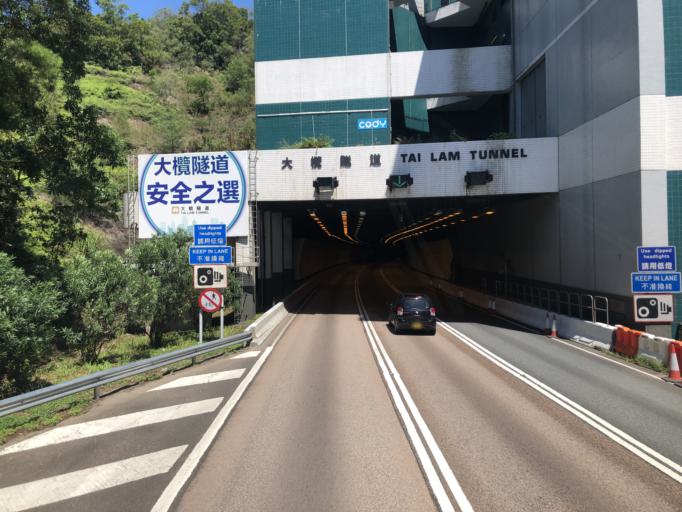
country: HK
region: Tsuen Wan
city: Tsuen Wan
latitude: 22.3751
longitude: 114.0672
